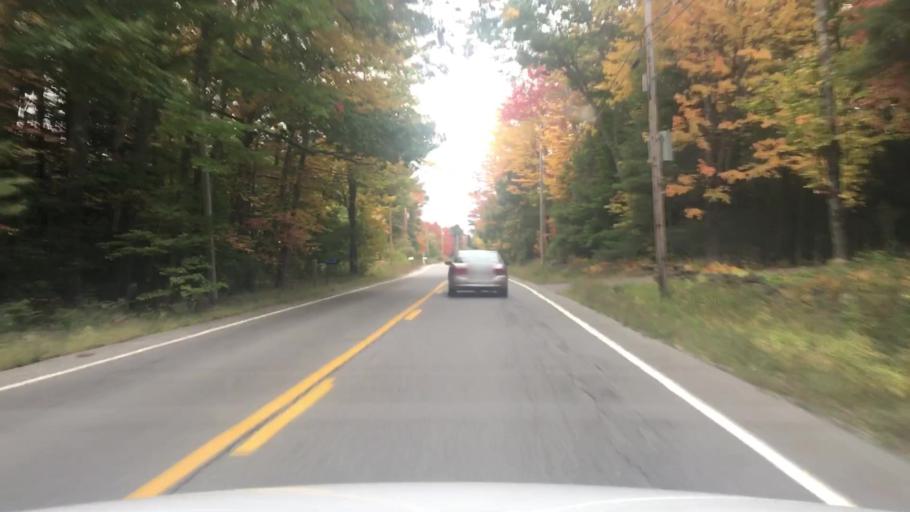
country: US
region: Maine
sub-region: Kennebec County
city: Oakland
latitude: 44.5385
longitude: -69.7923
